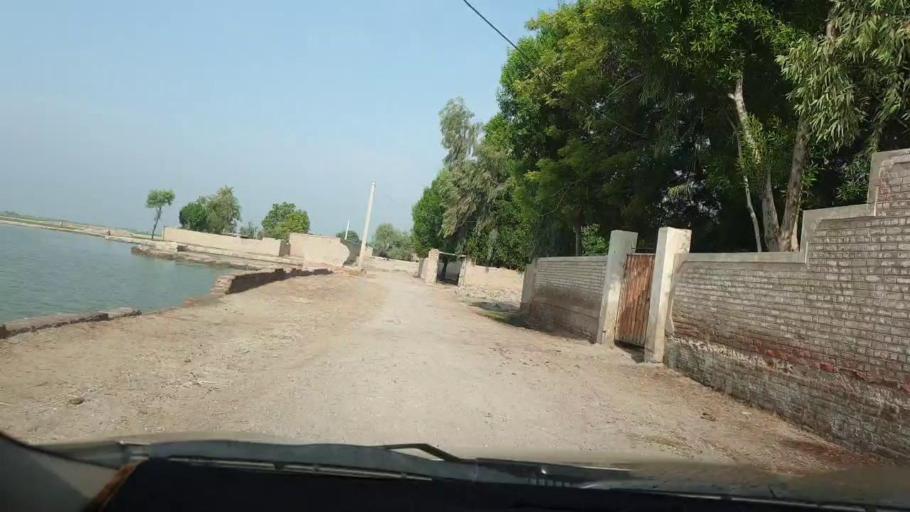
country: PK
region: Sindh
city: Goth Garelo
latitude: 27.4660
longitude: 68.0842
